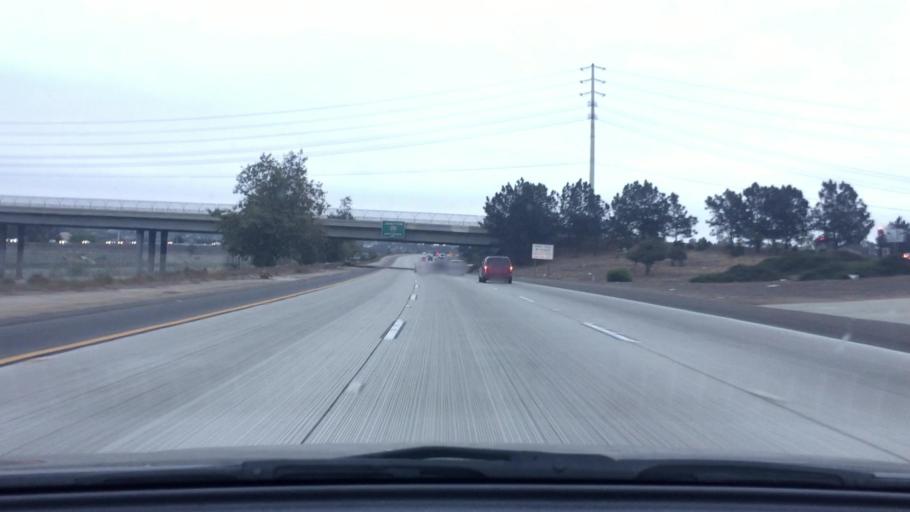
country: US
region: California
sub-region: San Diego County
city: Chula Vista
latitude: 32.6539
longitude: -117.0912
